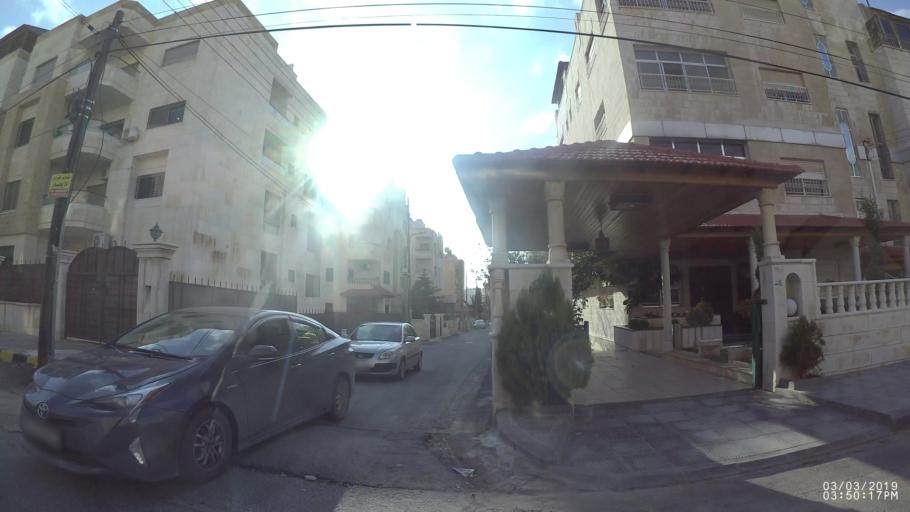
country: JO
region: Amman
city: Al Jubayhah
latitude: 31.9806
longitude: 35.8756
